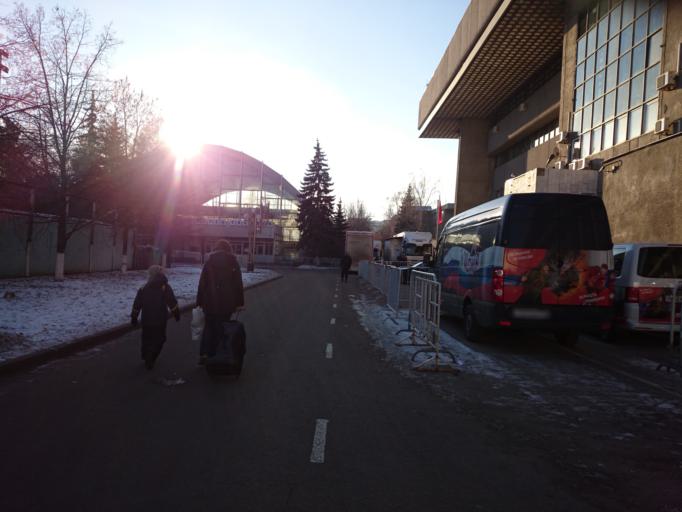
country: RU
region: Moscow
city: Sokol
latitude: 55.7945
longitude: 37.5387
